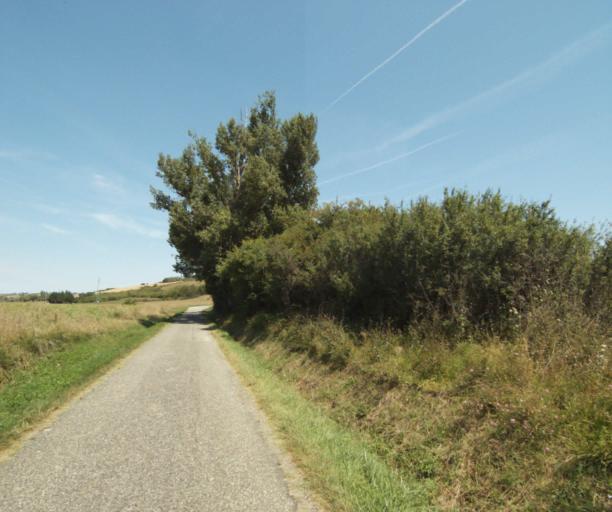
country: FR
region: Midi-Pyrenees
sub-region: Departement de l'Ariege
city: Lezat-sur-Leze
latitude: 43.2779
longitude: 1.3566
